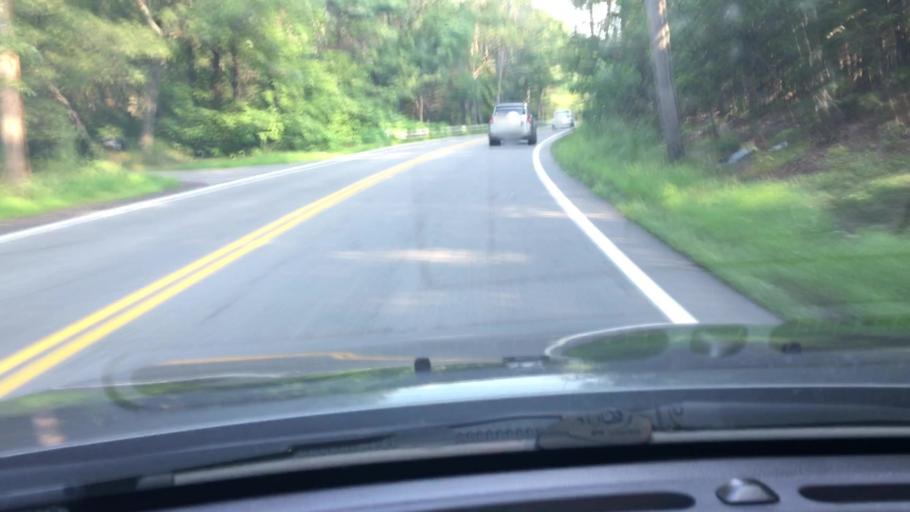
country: US
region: Massachusetts
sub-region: Worcester County
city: Westborough
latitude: 42.2497
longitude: -71.5844
